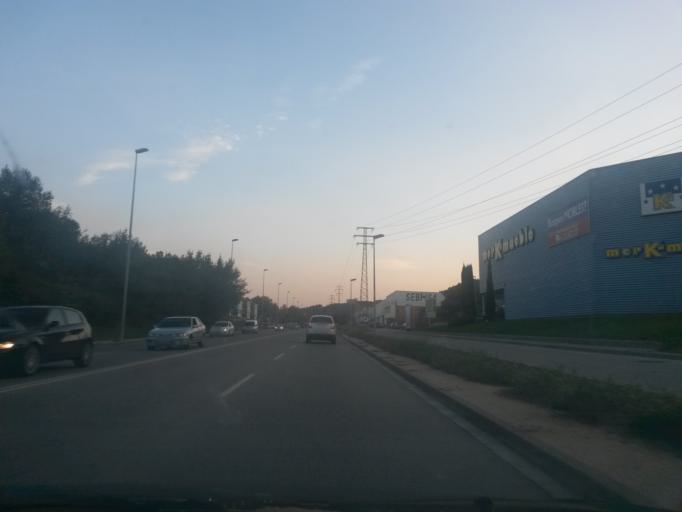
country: ES
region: Catalonia
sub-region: Provincia de Girona
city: Sarria de Ter
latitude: 42.0071
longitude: 2.8166
